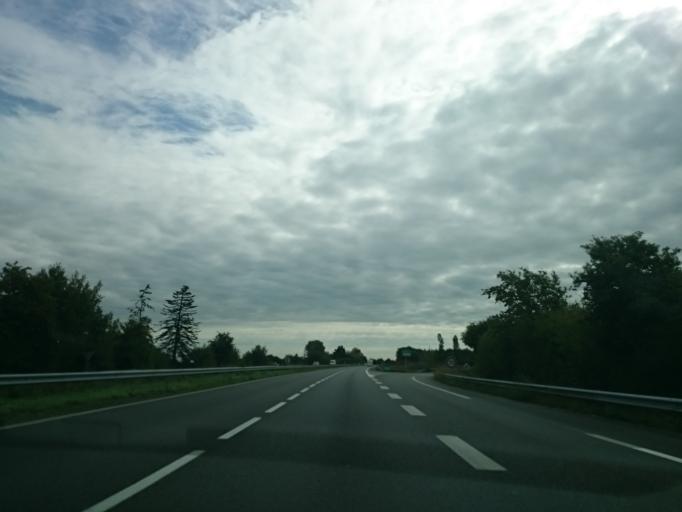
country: FR
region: Pays de la Loire
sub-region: Departement de la Loire-Atlantique
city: Pontchateau
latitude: 47.4476
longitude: -2.0956
